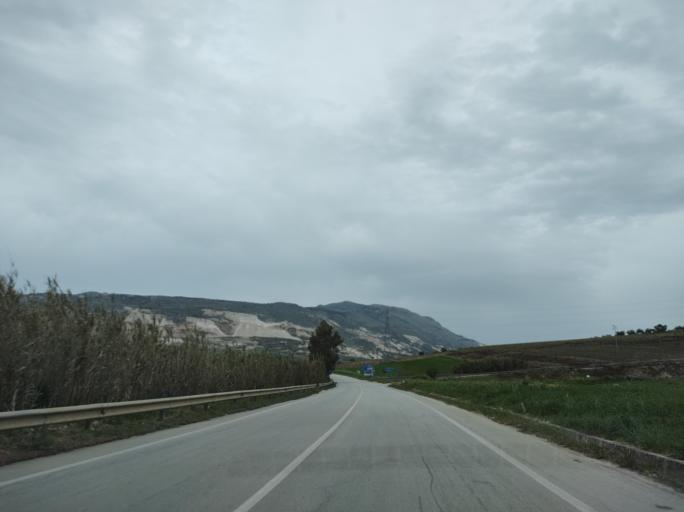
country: IT
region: Sicily
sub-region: Trapani
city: Custonaci
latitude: 38.0417
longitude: 12.6816
